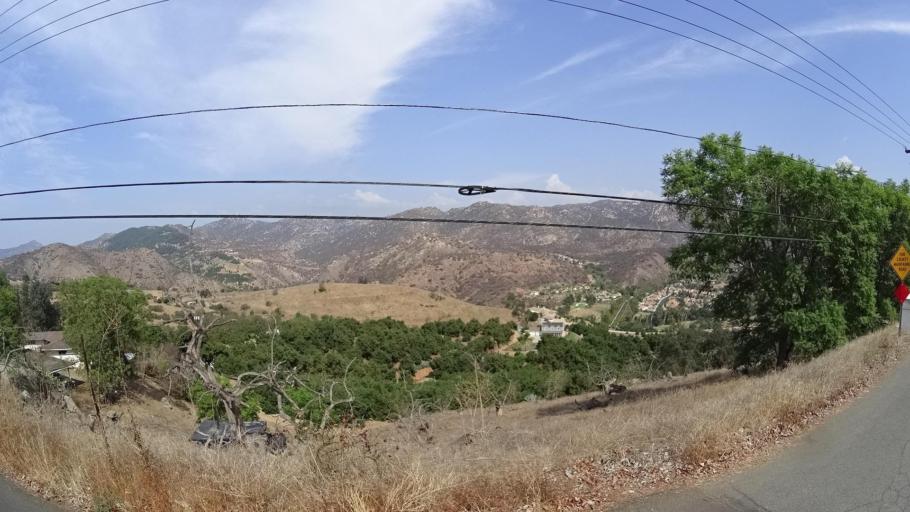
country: US
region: California
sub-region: San Diego County
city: Escondido
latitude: 33.1214
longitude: -117.0214
